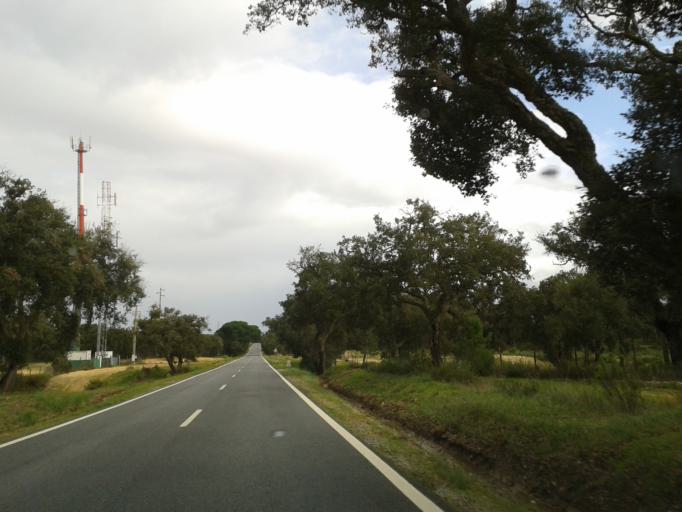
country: PT
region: Santarem
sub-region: Benavente
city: Poceirao
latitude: 38.8136
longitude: -8.7876
